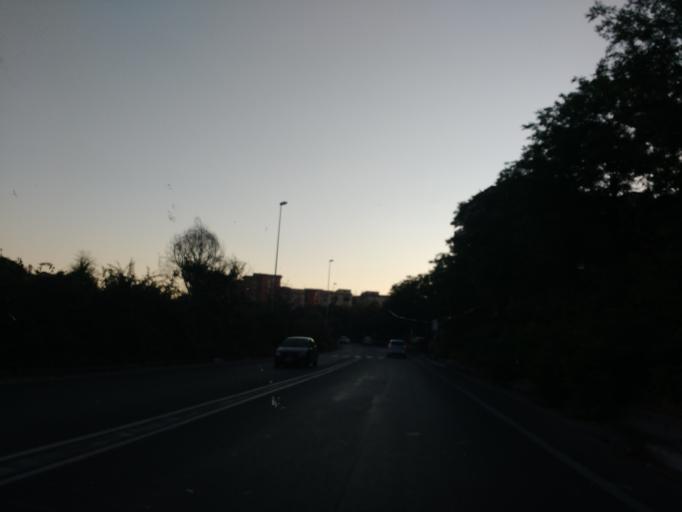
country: IT
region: Latium
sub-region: Citta metropolitana di Roma Capitale
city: Setteville
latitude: 41.9425
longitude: 12.6551
